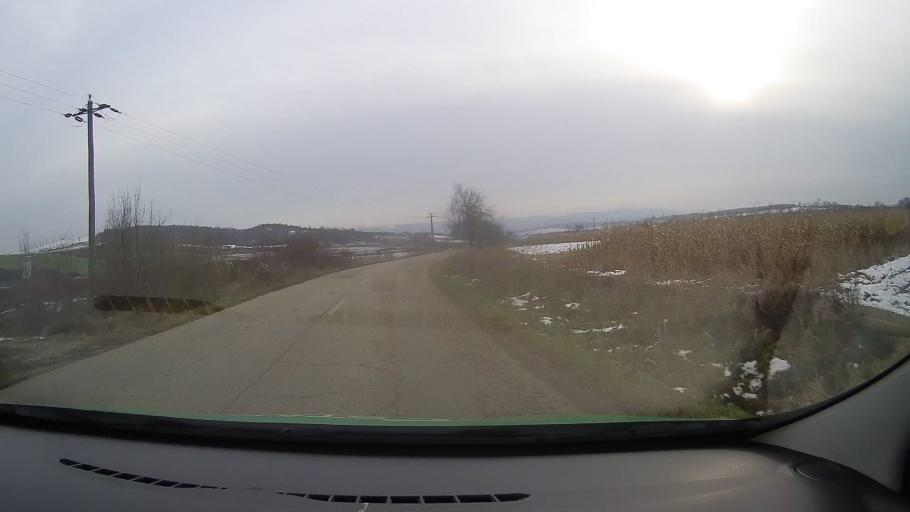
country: RO
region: Hunedoara
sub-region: Comuna Romos
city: Romos
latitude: 45.8640
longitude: 23.2739
